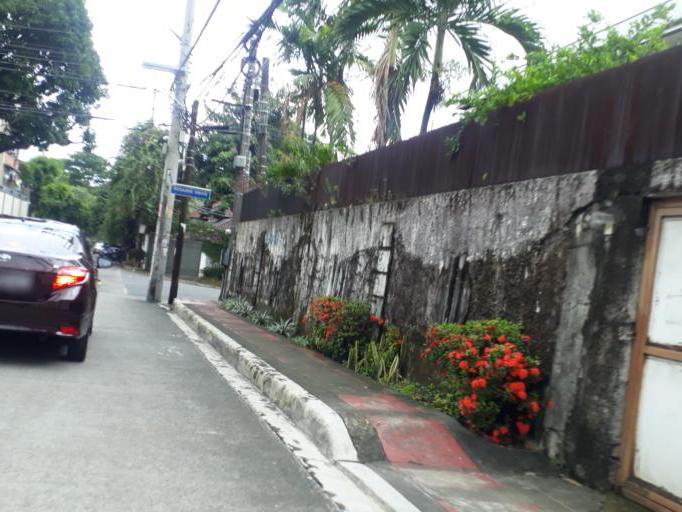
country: PH
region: Metro Manila
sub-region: San Juan
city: San Juan
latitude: 14.6216
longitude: 121.0415
